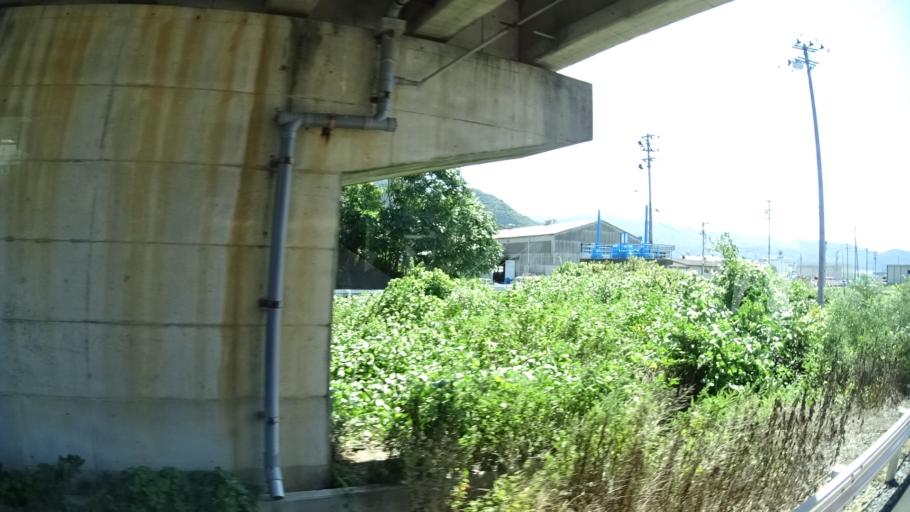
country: JP
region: Iwate
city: Ofunato
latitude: 39.0789
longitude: 141.7141
